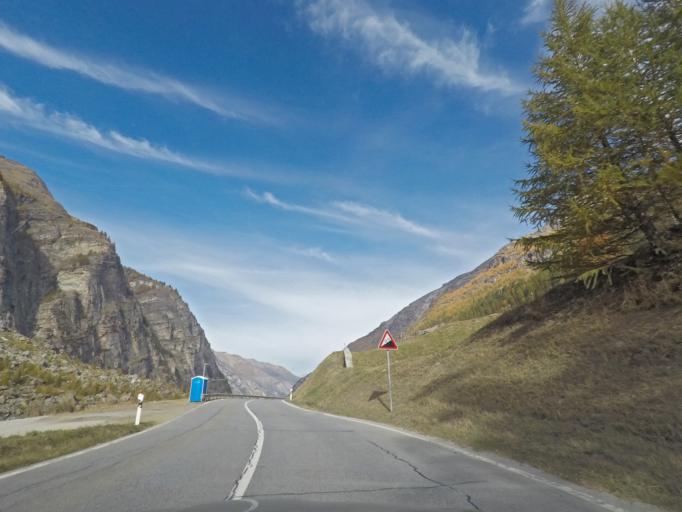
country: CH
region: Valais
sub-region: Visp District
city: Sankt Niklaus
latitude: 46.1070
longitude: 7.7842
